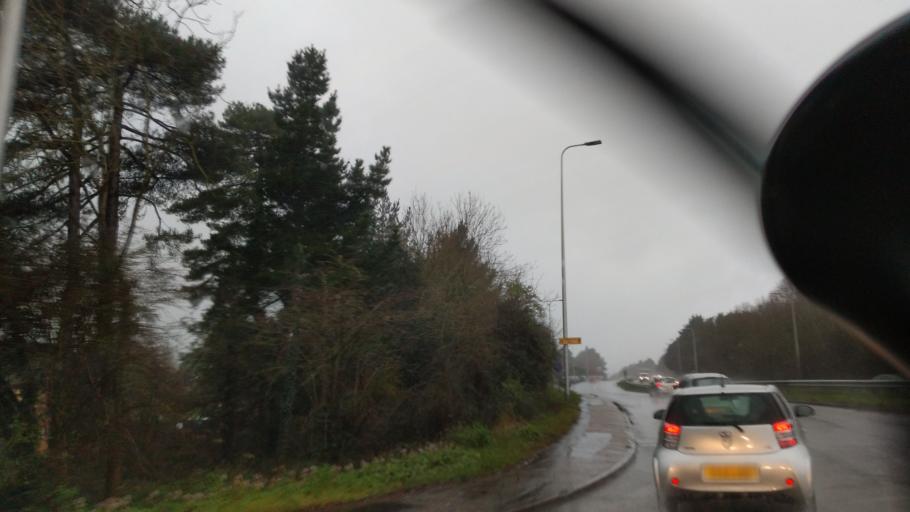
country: GB
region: England
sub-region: West Sussex
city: Fontwell
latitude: 50.8555
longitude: -0.6512
